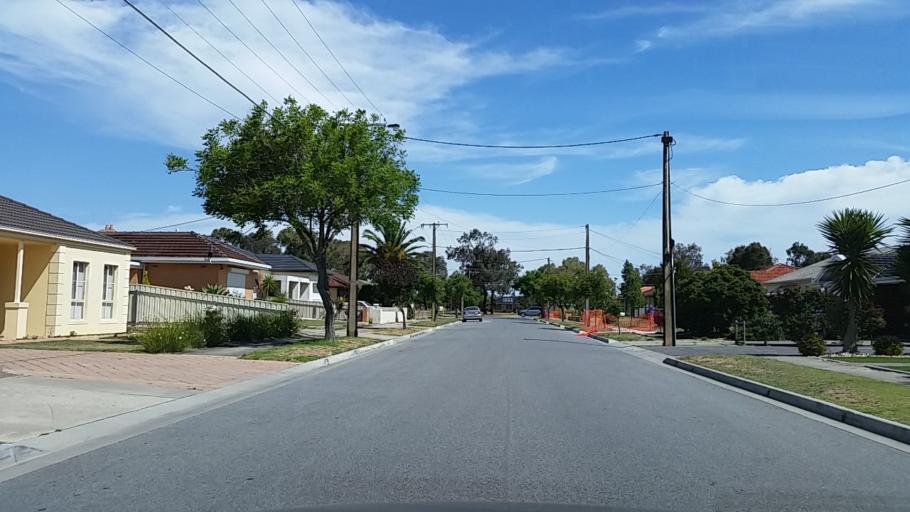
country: AU
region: South Australia
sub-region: Charles Sturt
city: Seaton
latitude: -34.9081
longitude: 138.5110
